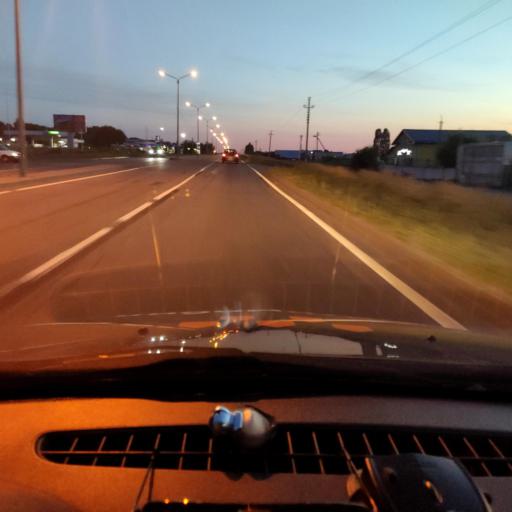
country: RU
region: Belgorod
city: Gubkin
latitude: 51.2650
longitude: 37.5515
